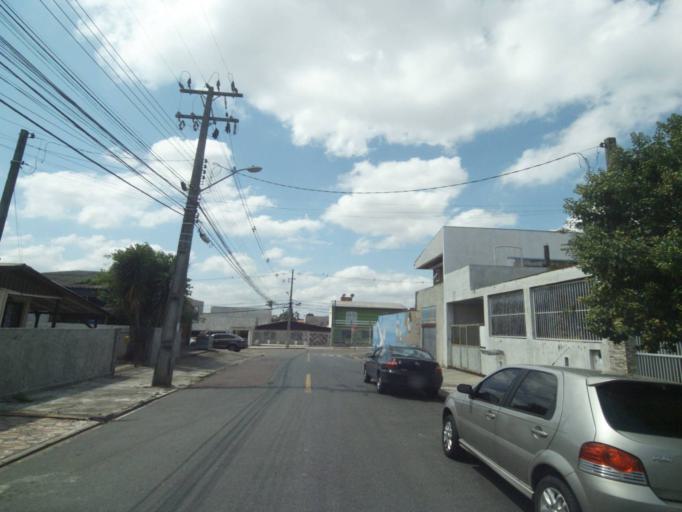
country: BR
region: Parana
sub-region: Curitiba
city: Curitiba
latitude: -25.5124
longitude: -49.3215
